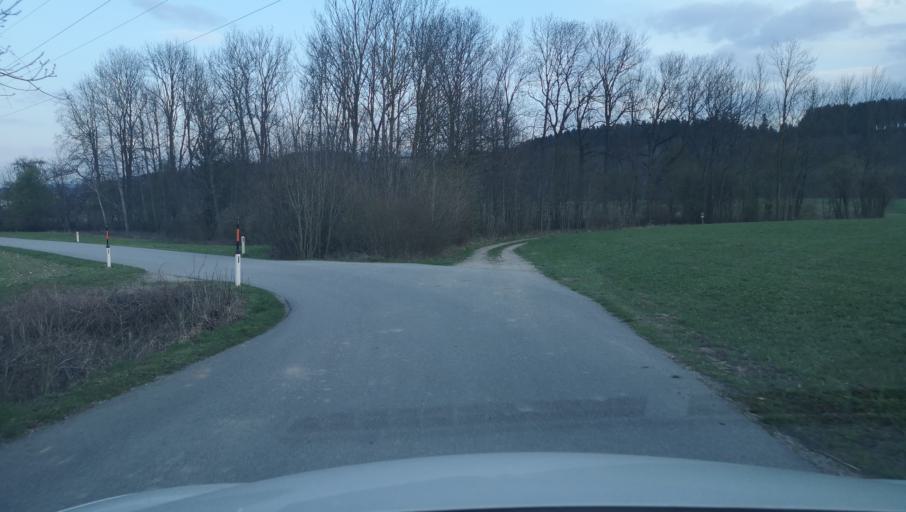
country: AT
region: Lower Austria
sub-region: Politischer Bezirk Amstetten
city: Amstetten
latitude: 48.1054
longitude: 14.8927
